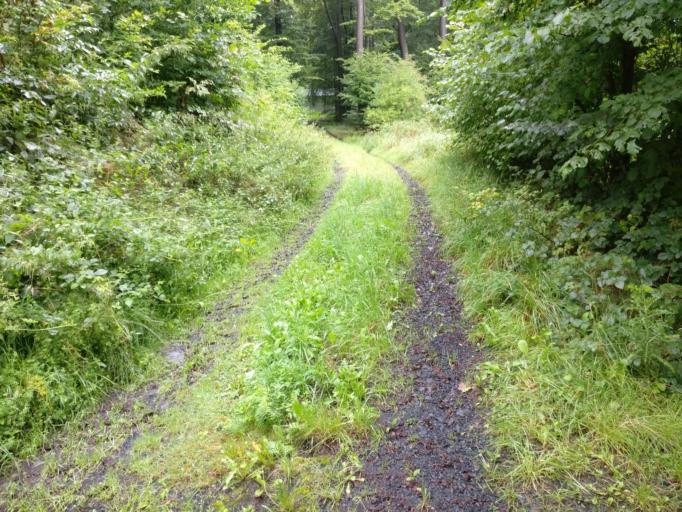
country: DE
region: Hesse
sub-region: Regierungsbezirk Giessen
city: Greifenstein
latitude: 50.6229
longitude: 8.2810
